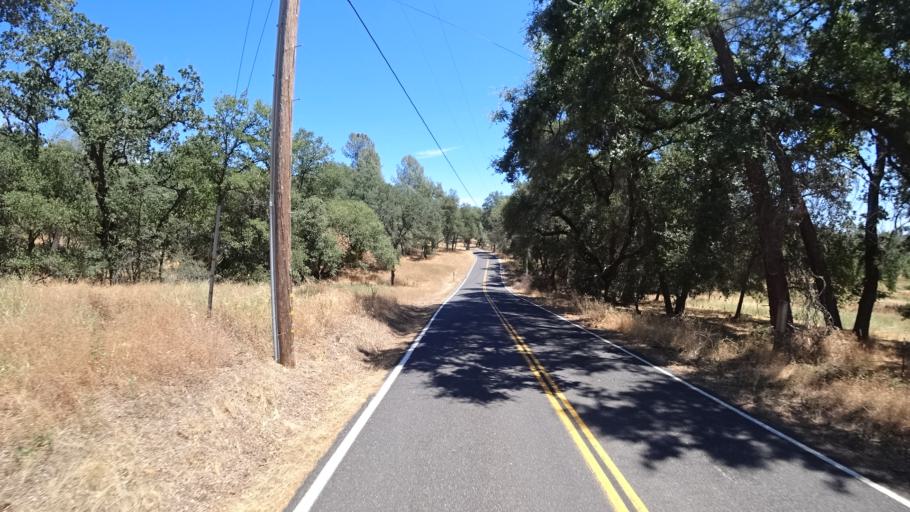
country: US
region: California
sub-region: Calaveras County
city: Mountain Ranch
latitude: 38.2245
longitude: -120.4880
